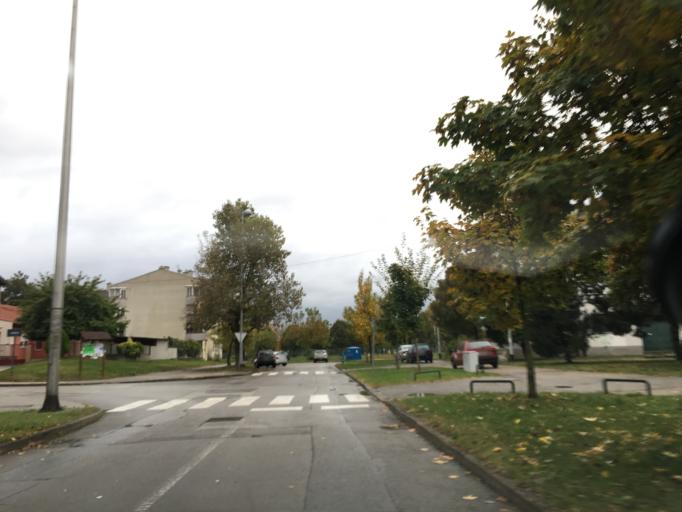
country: HR
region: Grad Zagreb
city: Jankomir
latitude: 45.7863
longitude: 15.9213
